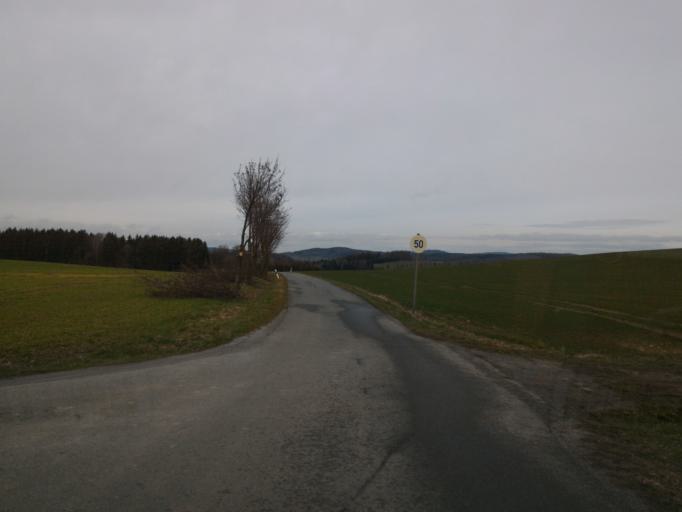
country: DE
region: Saxony
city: Friedersdorf
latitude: 51.0101
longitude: 14.5521
